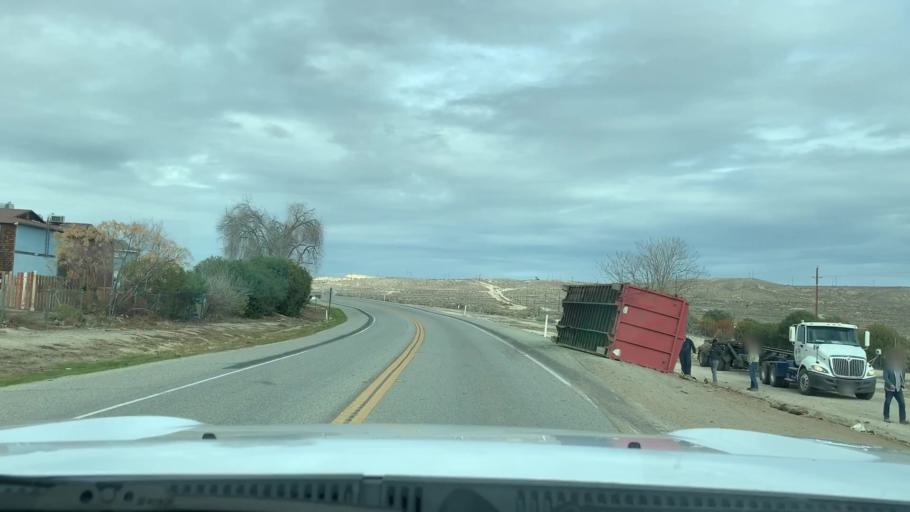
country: US
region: California
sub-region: Kern County
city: Ford City
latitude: 35.1551
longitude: -119.4479
